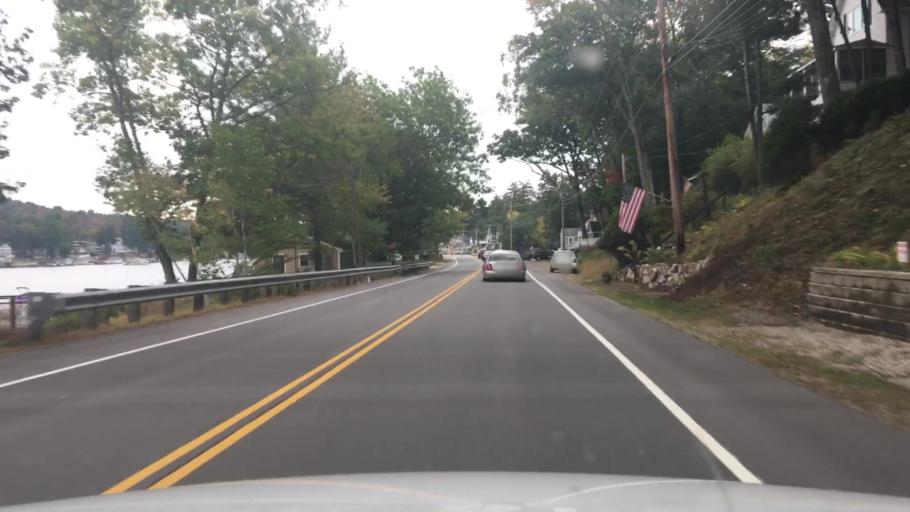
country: US
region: New Hampshire
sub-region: Strafford County
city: New Durham
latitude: 43.4781
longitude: -71.2409
